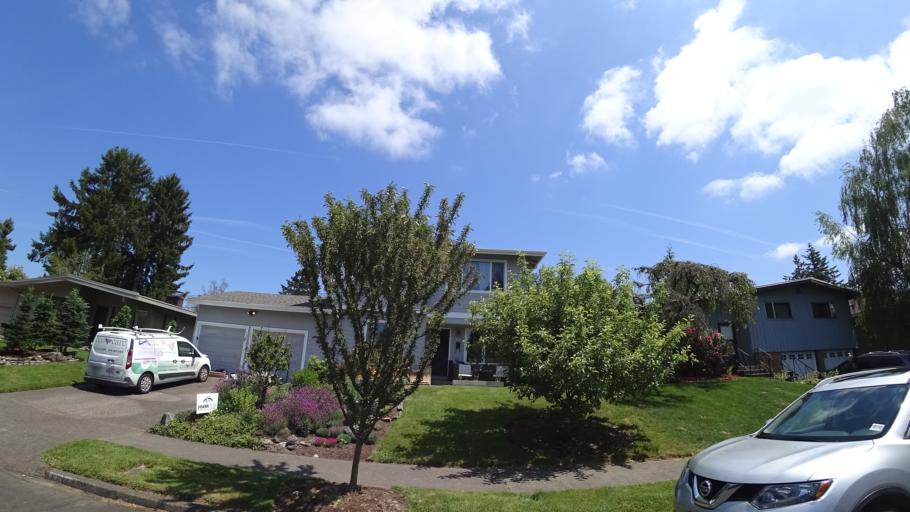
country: US
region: Oregon
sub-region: Multnomah County
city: Portland
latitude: 45.4750
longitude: -122.6895
